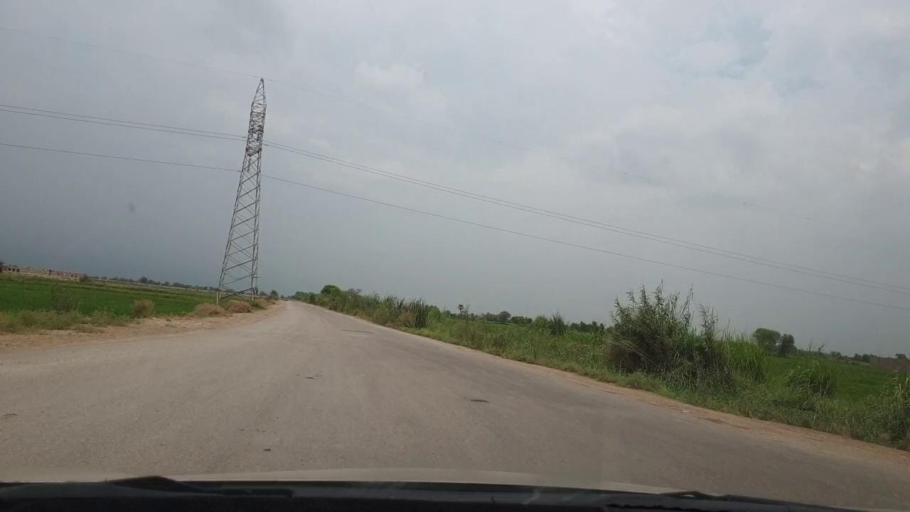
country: PK
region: Sindh
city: Ratodero
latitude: 27.8041
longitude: 68.3096
